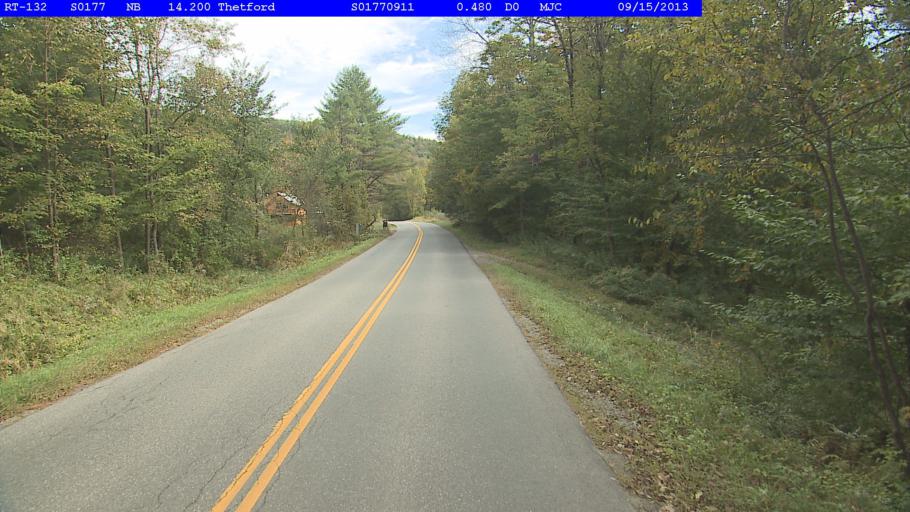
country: US
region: New Hampshire
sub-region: Grafton County
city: Hanover
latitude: 43.8327
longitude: -72.3124
